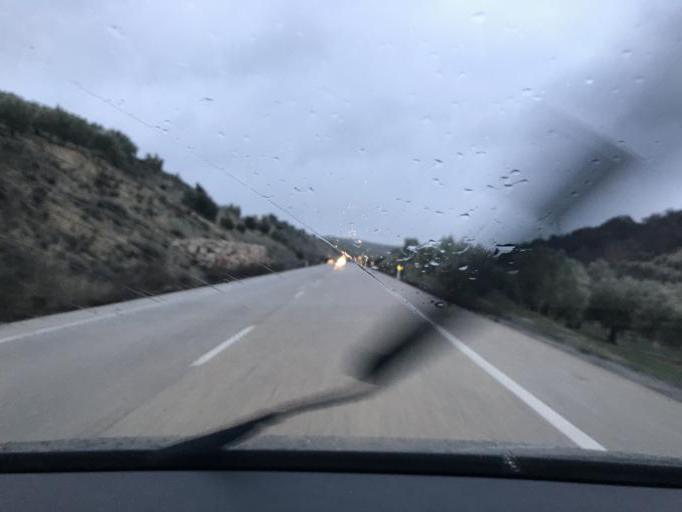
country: ES
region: Andalusia
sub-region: Provincia de Granada
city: Campotejar
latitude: 37.4618
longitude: -3.6028
